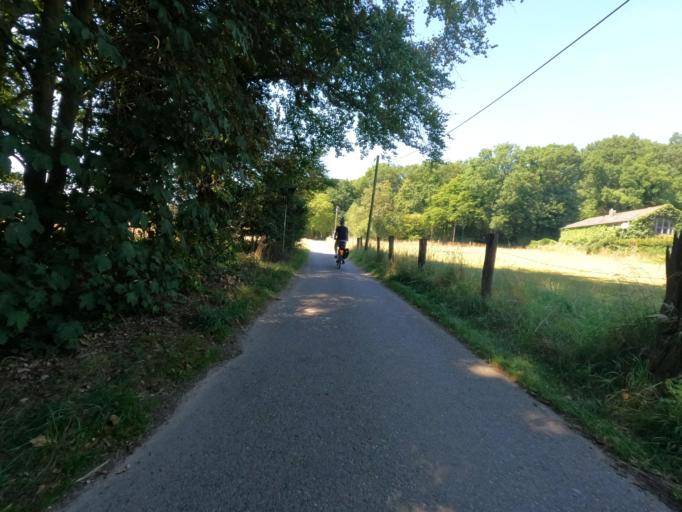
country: DE
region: North Rhine-Westphalia
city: Wegberg
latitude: 51.1634
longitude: 6.2714
